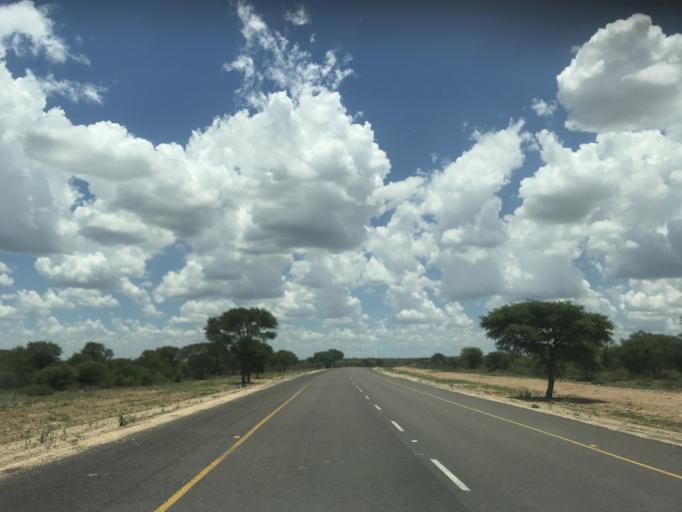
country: BW
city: Mabuli
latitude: -25.7954
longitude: 24.8861
